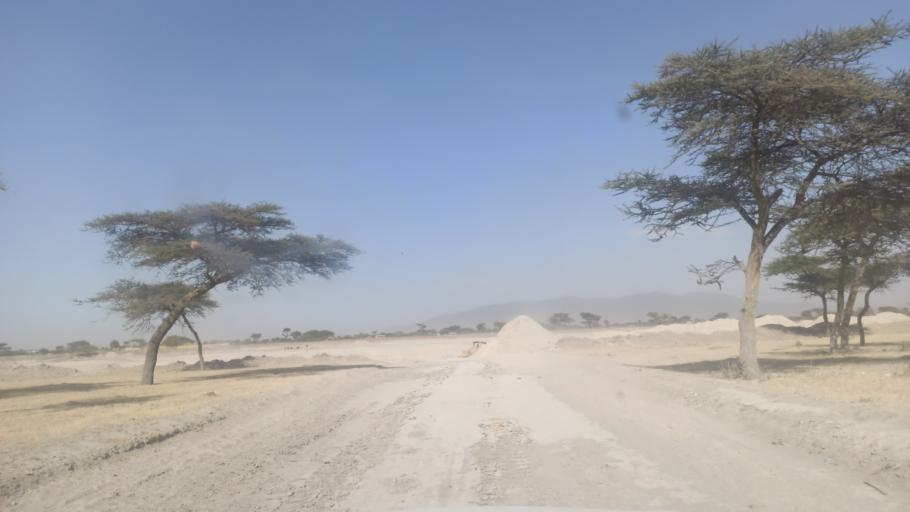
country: ET
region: Oromiya
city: Ziway
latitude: 7.6907
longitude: 38.6632
